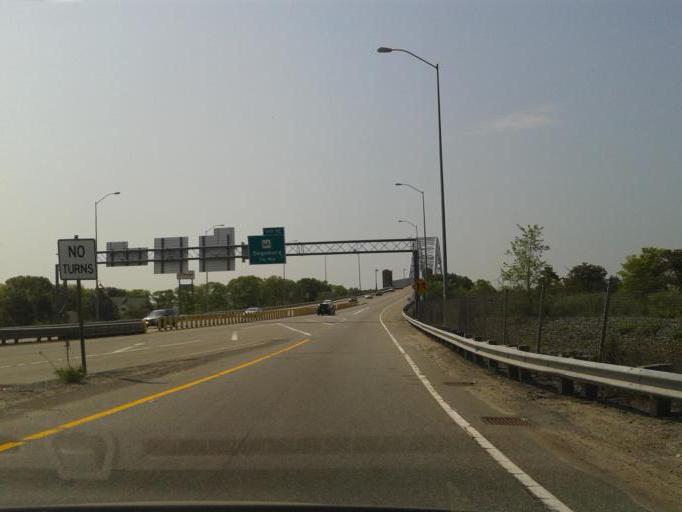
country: US
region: Massachusetts
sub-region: Barnstable County
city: Sagamore
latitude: 41.7810
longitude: -70.5437
